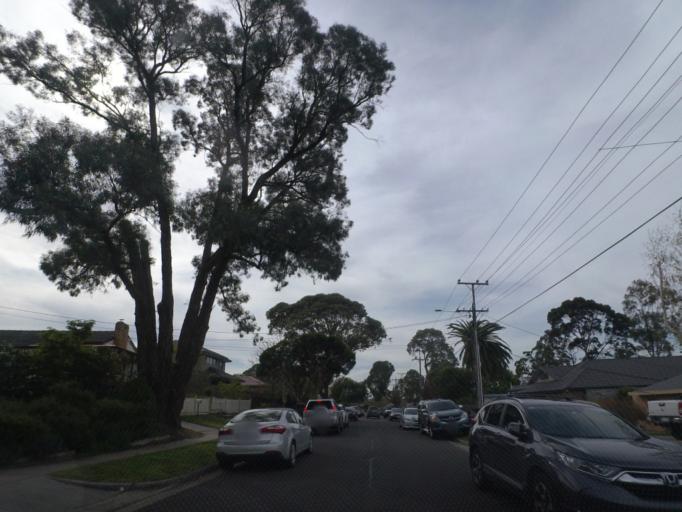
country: AU
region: Victoria
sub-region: Whitehorse
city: Vermont
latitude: -37.8284
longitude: 145.2030
